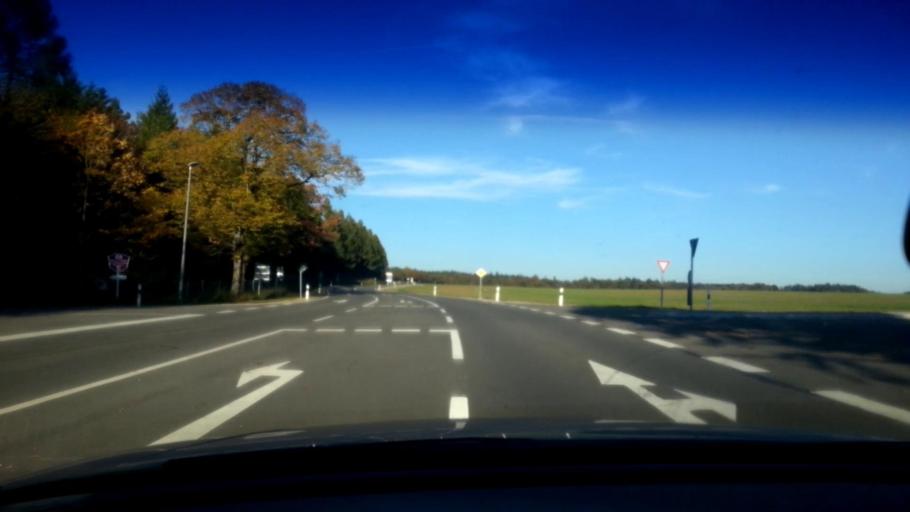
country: DE
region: Bavaria
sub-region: Upper Franconia
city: Heiligenstadt
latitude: 49.8737
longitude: 11.1847
